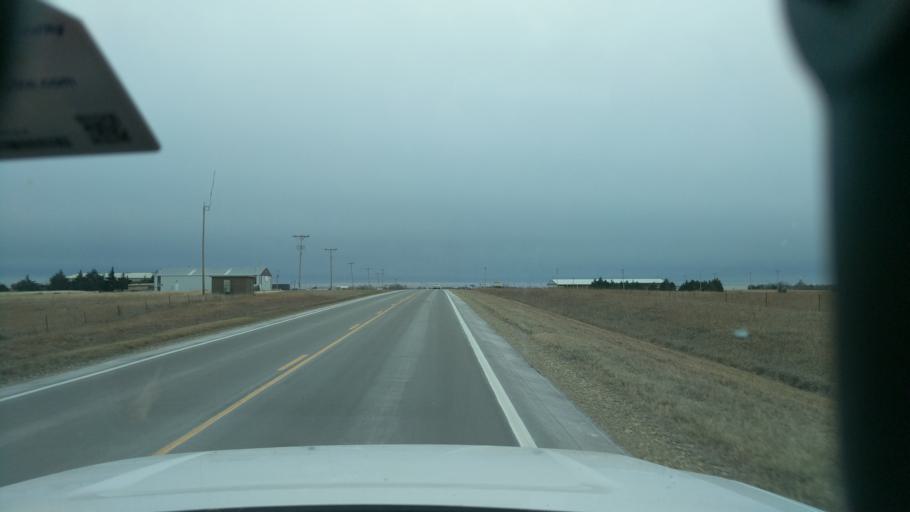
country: US
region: Kansas
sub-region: Dickinson County
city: Herington
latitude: 38.6854
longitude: -96.9306
